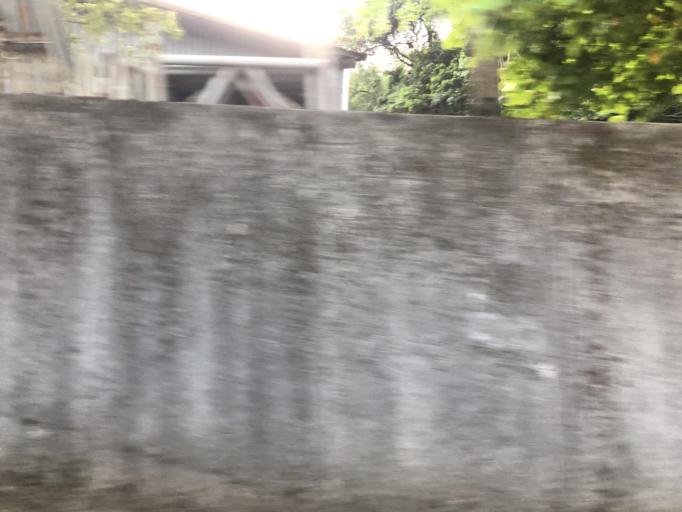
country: TW
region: Taiwan
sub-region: Keelung
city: Keelung
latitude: 25.1976
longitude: 121.6466
